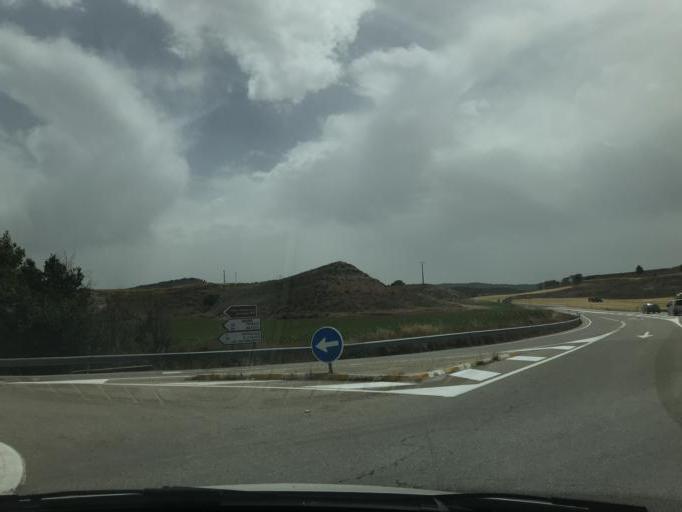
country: ES
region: Castille-La Mancha
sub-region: Provincia de Cuenca
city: Villar de Domingo Garcia
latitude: 40.2448
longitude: -2.3029
